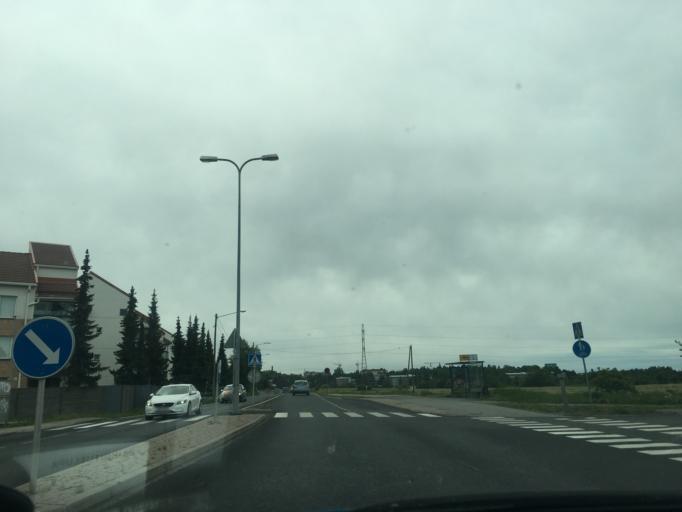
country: FI
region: Varsinais-Suomi
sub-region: Turku
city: Turku
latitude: 60.4693
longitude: 22.3069
